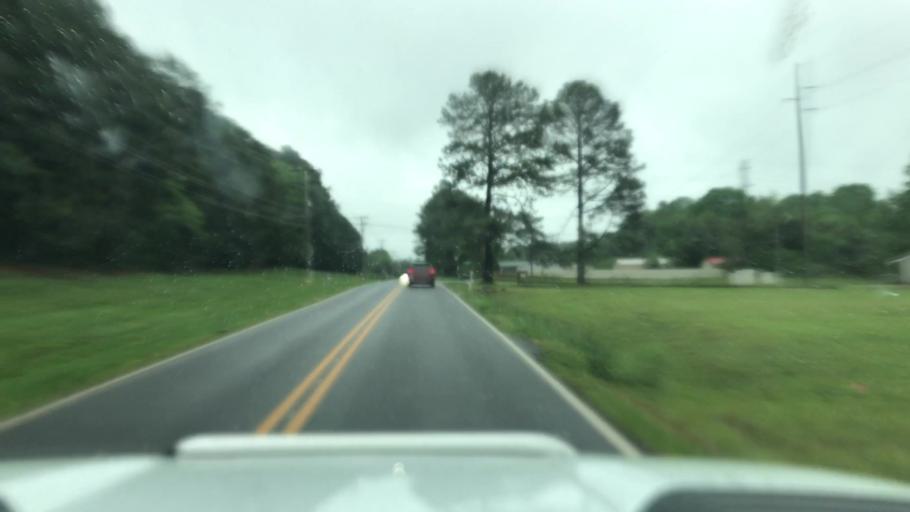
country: US
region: North Carolina
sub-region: Mecklenburg County
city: Huntersville
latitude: 35.3884
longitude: -80.8801
